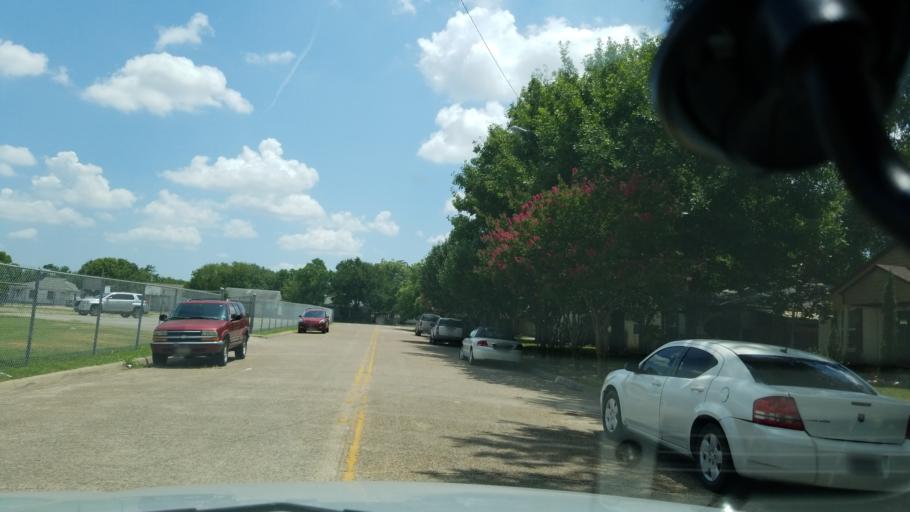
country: US
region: Texas
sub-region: Dallas County
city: Cockrell Hill
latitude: 32.7283
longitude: -96.8710
